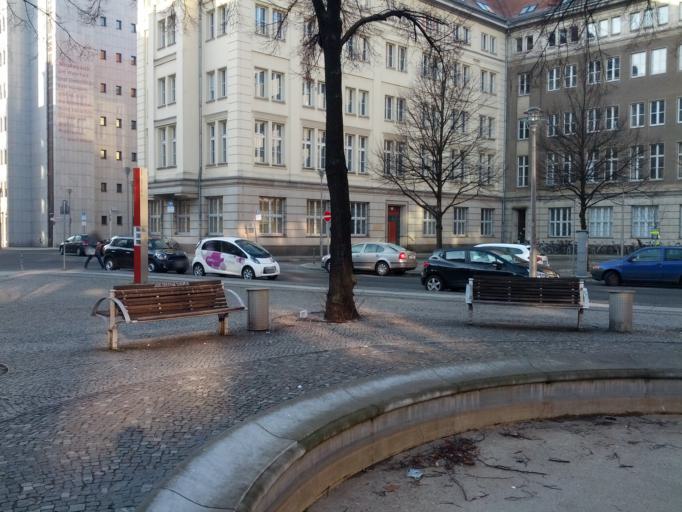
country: DE
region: Berlin
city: Mitte
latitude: 52.5129
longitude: 13.3965
